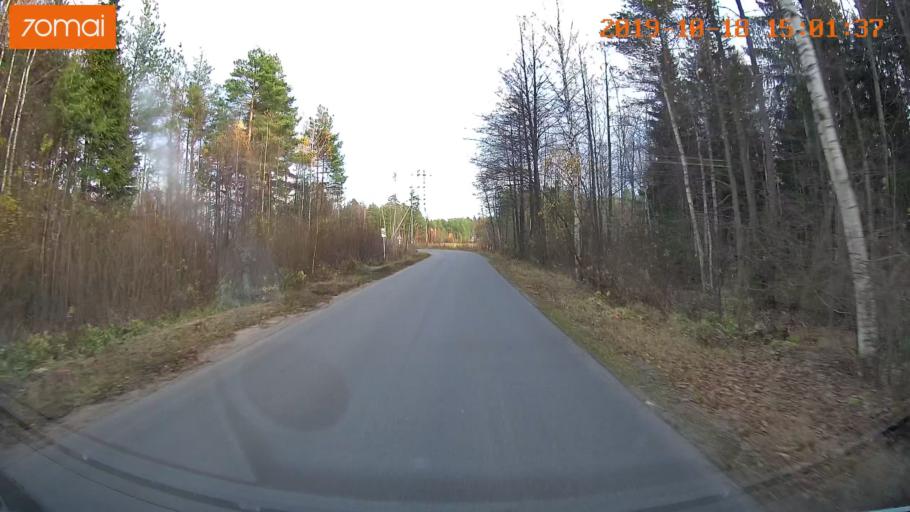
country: RU
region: Vladimir
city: Gus'-Khrustal'nyy
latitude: 55.5003
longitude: 40.6070
